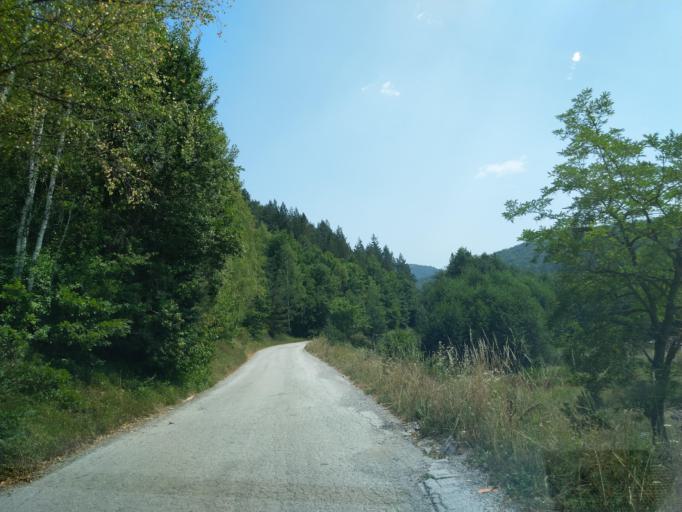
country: RS
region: Central Serbia
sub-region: Zlatiborski Okrug
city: Prijepolje
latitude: 43.3325
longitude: 19.5630
